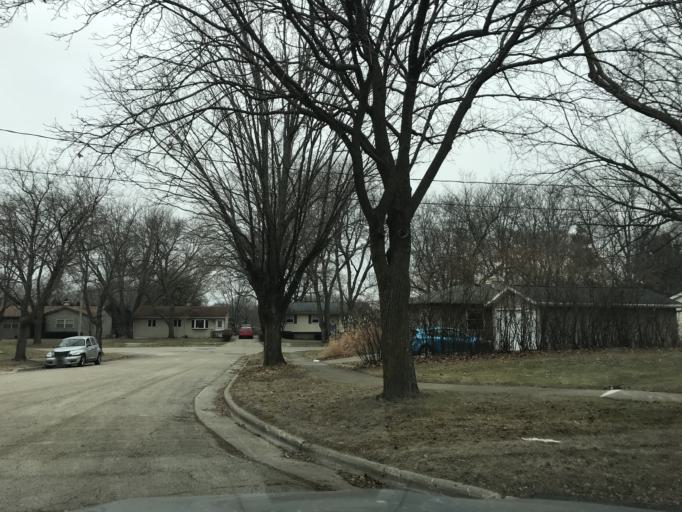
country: US
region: Wisconsin
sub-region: Dane County
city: Monona
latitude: 43.0955
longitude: -89.3070
